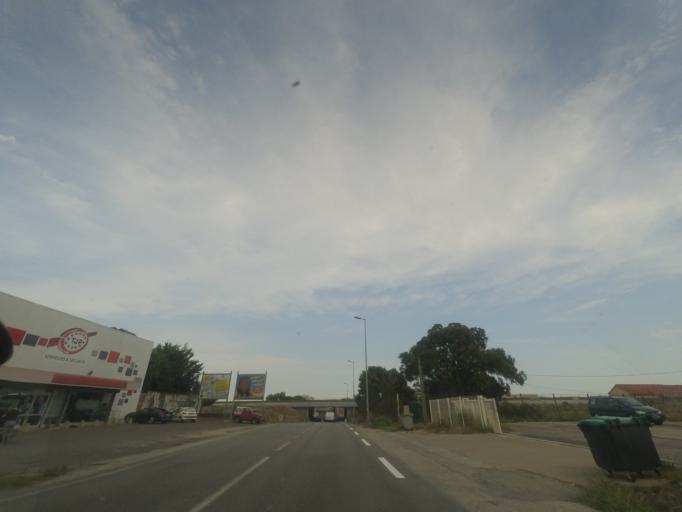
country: FR
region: Languedoc-Roussillon
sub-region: Departement des Pyrenees-Orientales
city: Saint-Esteve
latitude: 42.6958
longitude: 2.8608
